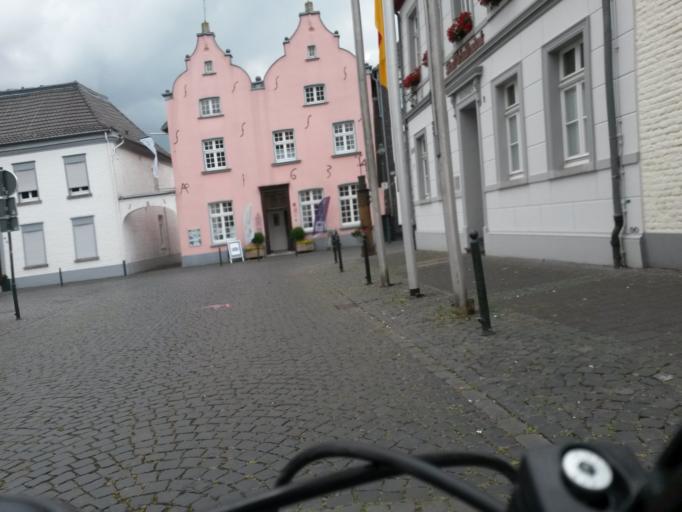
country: DE
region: North Rhine-Westphalia
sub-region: Regierungsbezirk Dusseldorf
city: Wachtendonk
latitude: 51.4071
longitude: 6.3355
